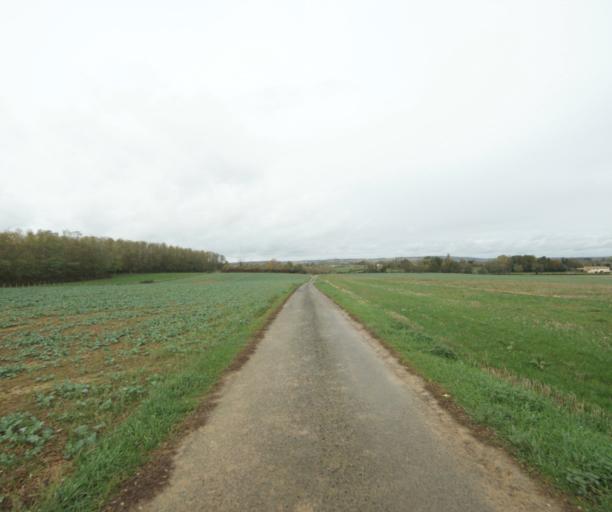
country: FR
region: Rhone-Alpes
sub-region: Departement de l'Ain
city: Pont-de-Vaux
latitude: 46.4552
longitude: 4.8812
